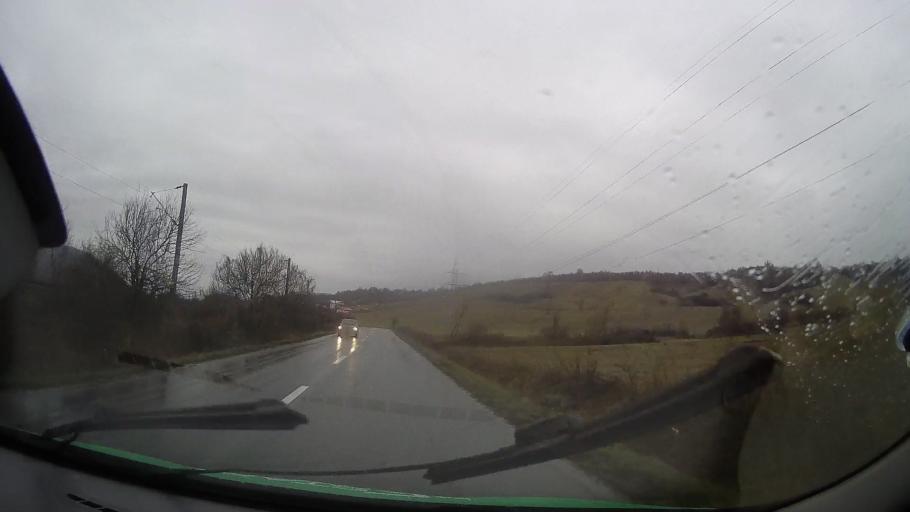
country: RO
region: Bistrita-Nasaud
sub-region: Municipiul Bistrita
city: Viisoara
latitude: 47.0467
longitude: 24.4637
